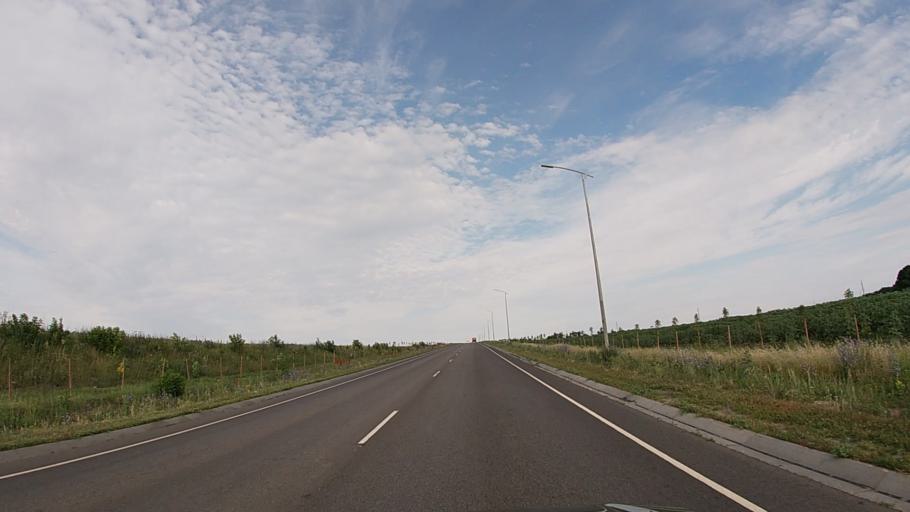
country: RU
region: Belgorod
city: Severnyy
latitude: 50.6647
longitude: 36.5138
